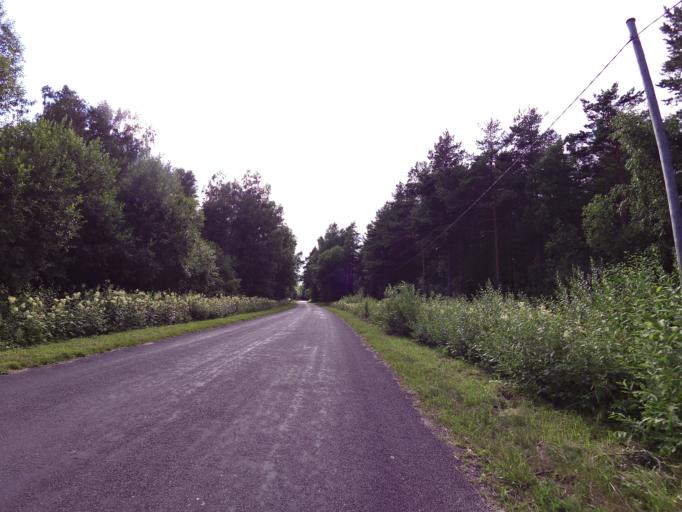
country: EE
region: Laeaene
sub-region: Vormsi vald
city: Hullo
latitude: 58.9849
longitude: 23.2917
